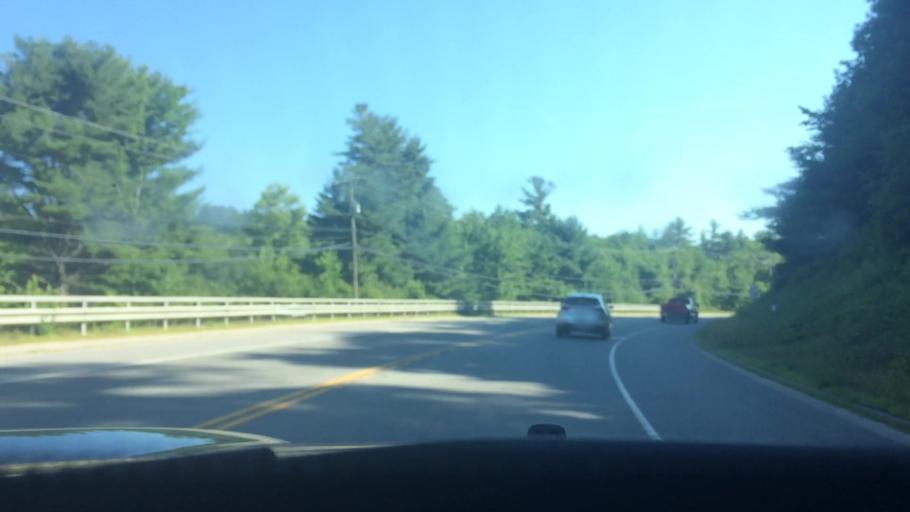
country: US
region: New Hampshire
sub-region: Hillsborough County
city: Peterborough
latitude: 42.8973
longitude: -71.9425
